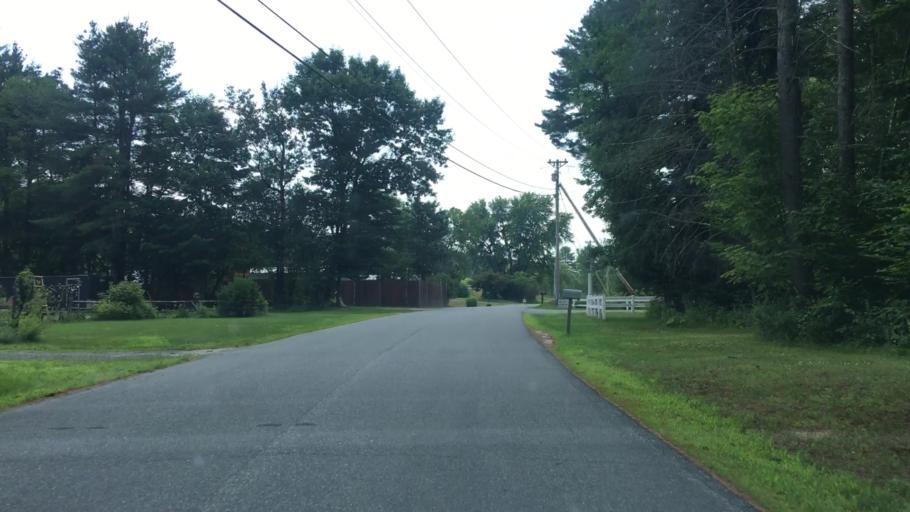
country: US
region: New Hampshire
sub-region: Grafton County
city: Enfield
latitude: 43.6781
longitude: -72.0955
